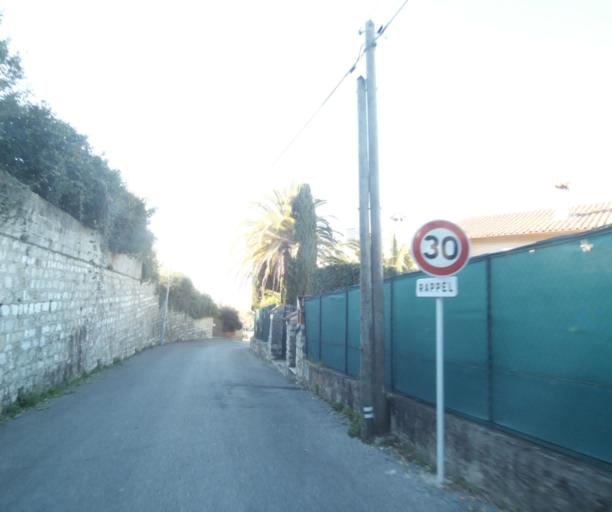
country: FR
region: Provence-Alpes-Cote d'Azur
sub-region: Departement des Alpes-Maritimes
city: Antibes
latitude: 43.5799
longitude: 7.1018
